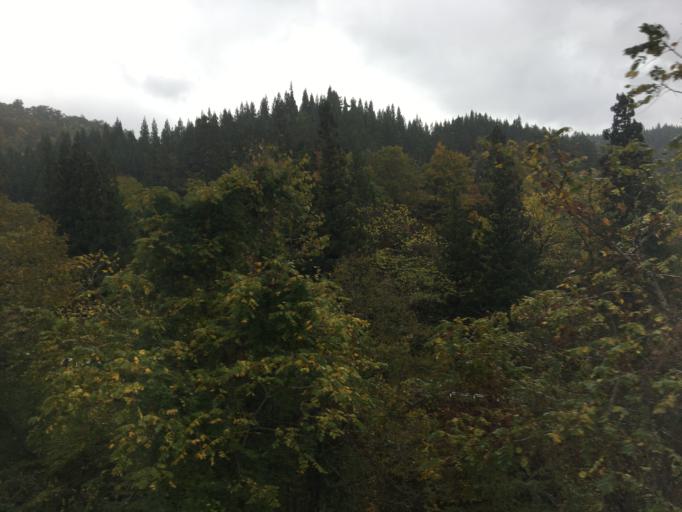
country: JP
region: Yamagata
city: Nagai
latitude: 38.0173
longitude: 139.9059
